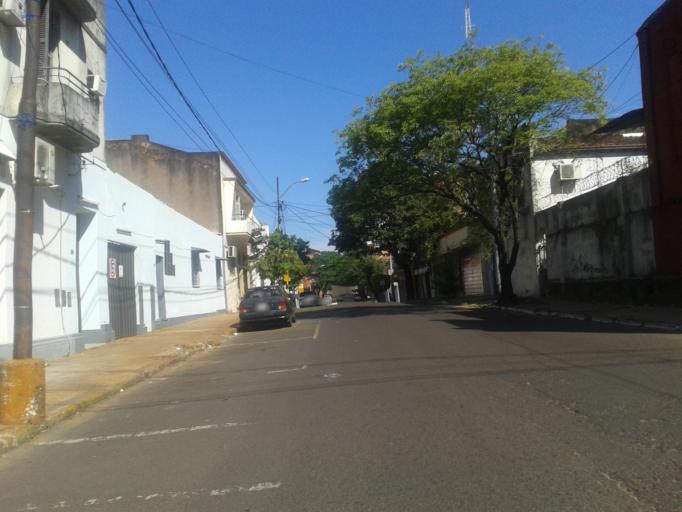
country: PY
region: Asuncion
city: Asuncion
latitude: -25.2897
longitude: -57.6385
